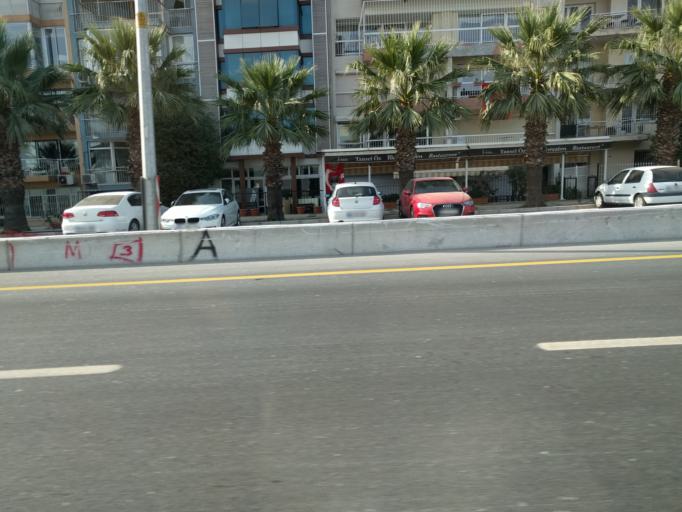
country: TR
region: Izmir
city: Izmir
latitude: 38.4097
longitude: 27.1134
